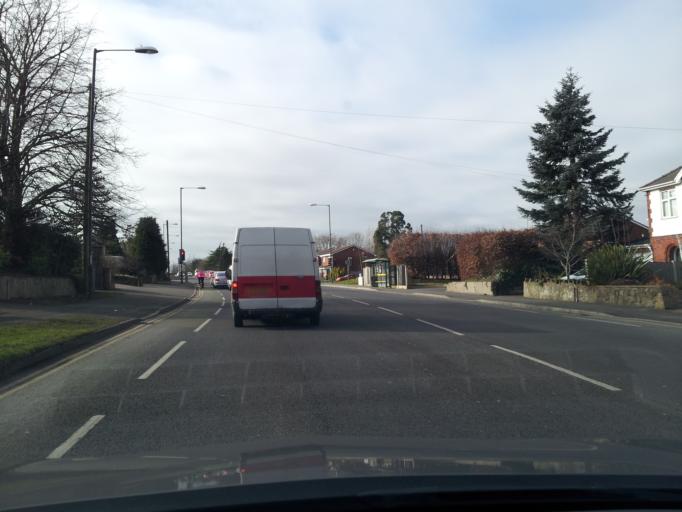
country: GB
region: England
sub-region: Derbyshire
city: Findern
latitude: 52.9103
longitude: -1.5221
